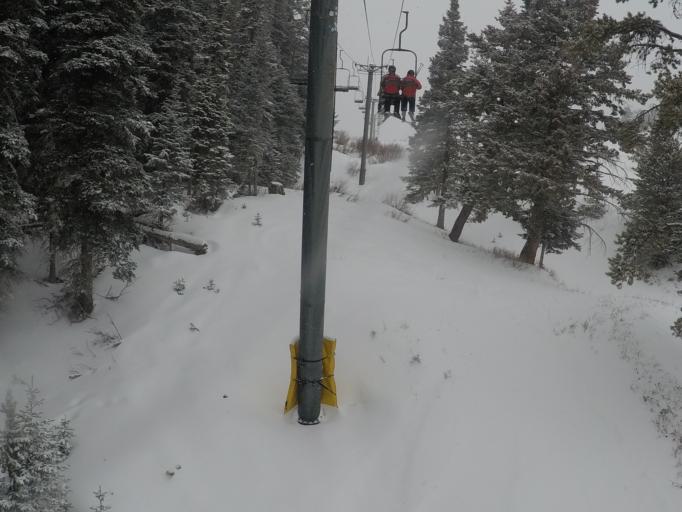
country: US
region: Montana
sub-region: Carbon County
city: Red Lodge
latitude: 45.1918
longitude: -109.3380
